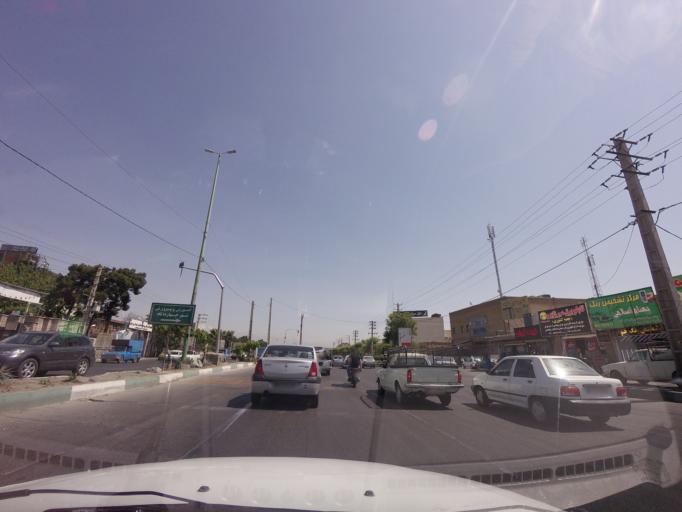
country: IR
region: Tehran
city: Eslamshahr
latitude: 35.6037
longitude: 51.3030
